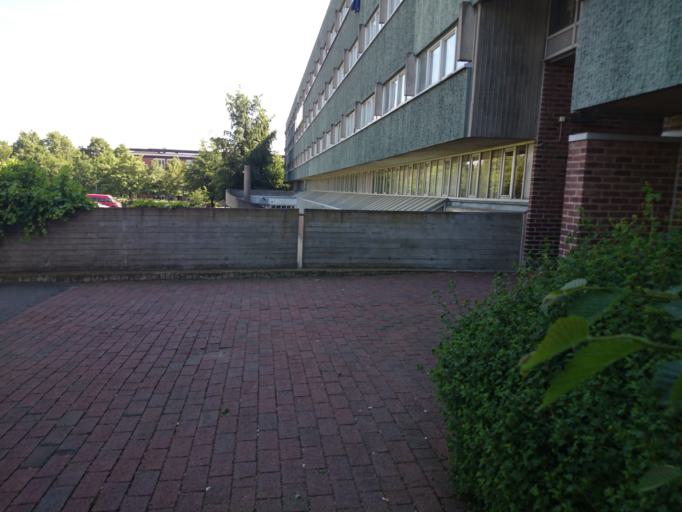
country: SE
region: Skane
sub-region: Lunds Kommun
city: Lund
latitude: 55.7105
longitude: 13.2171
